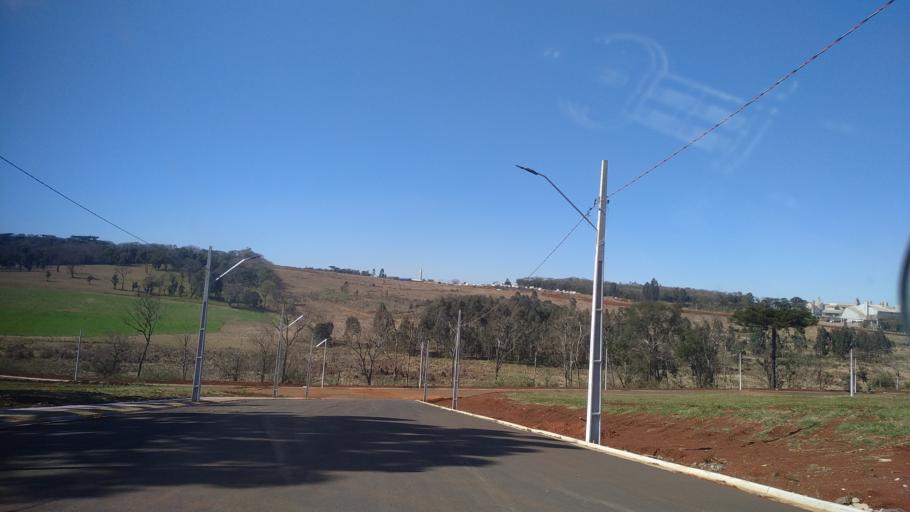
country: BR
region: Santa Catarina
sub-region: Chapeco
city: Chapeco
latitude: -27.0896
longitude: -52.7067
